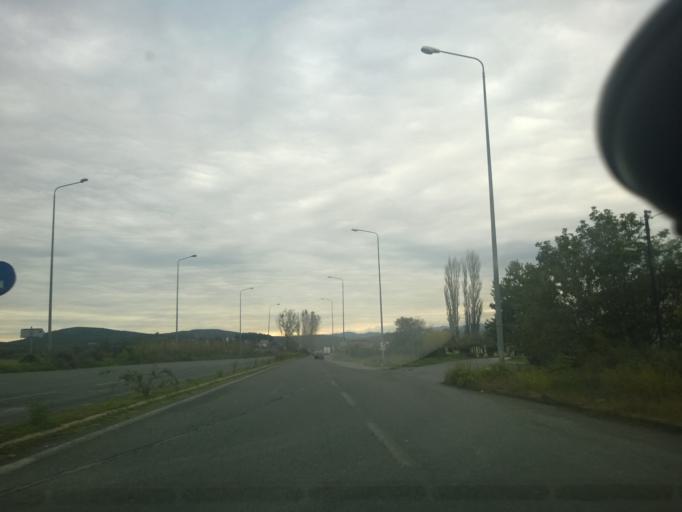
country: GR
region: Central Macedonia
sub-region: Nomos Pellis
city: Aridaia
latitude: 40.9340
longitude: 22.0844
